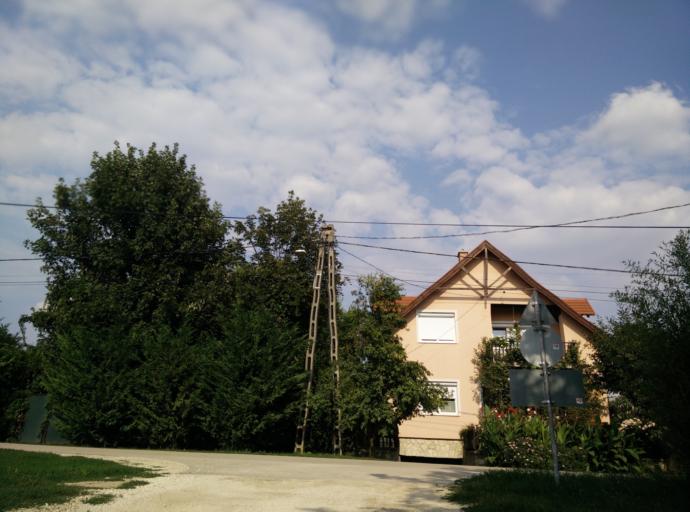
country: HU
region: Pest
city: Paty
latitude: 47.5183
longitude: 18.8239
